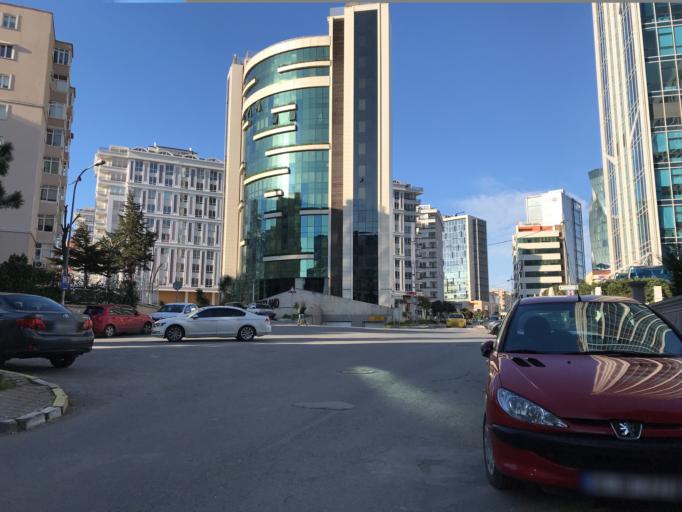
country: TR
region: Istanbul
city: Maltepe
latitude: 40.9352
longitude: 29.1341
